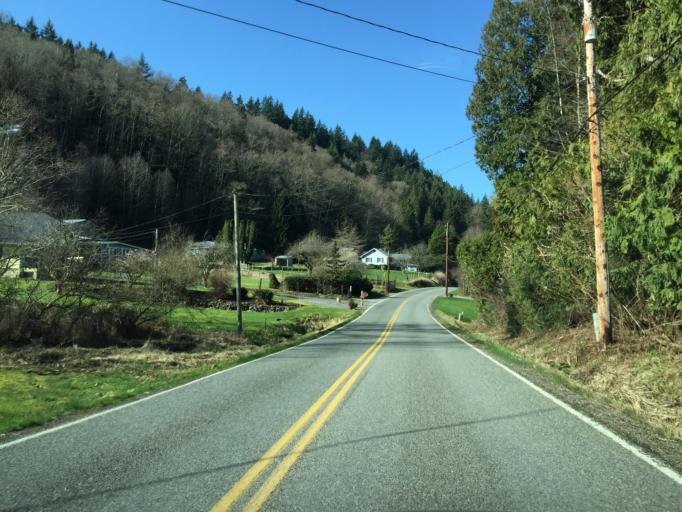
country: US
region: Washington
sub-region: Whatcom County
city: Bellingham
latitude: 48.6939
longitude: -122.4587
